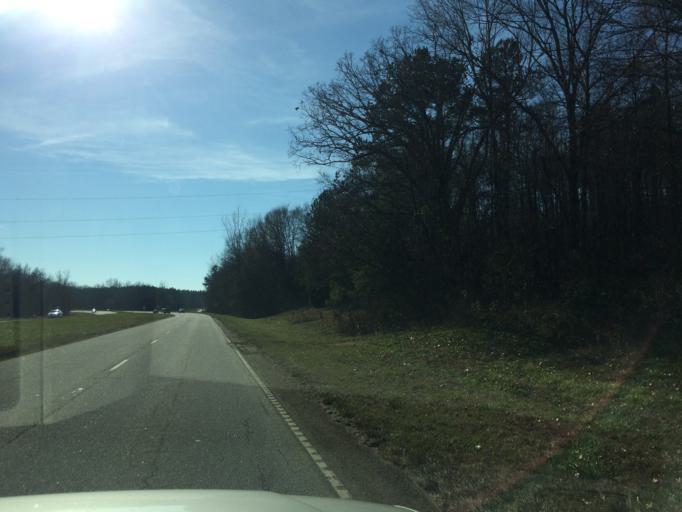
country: US
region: South Carolina
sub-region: Greenwood County
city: Greenwood
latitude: 34.2501
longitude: -82.0969
